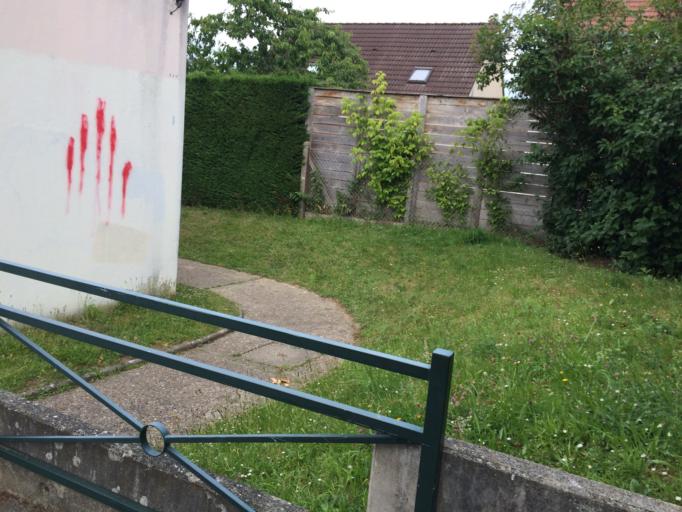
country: FR
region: Ile-de-France
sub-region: Departement de l'Essonne
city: Palaiseau
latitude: 48.7255
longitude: 2.2387
